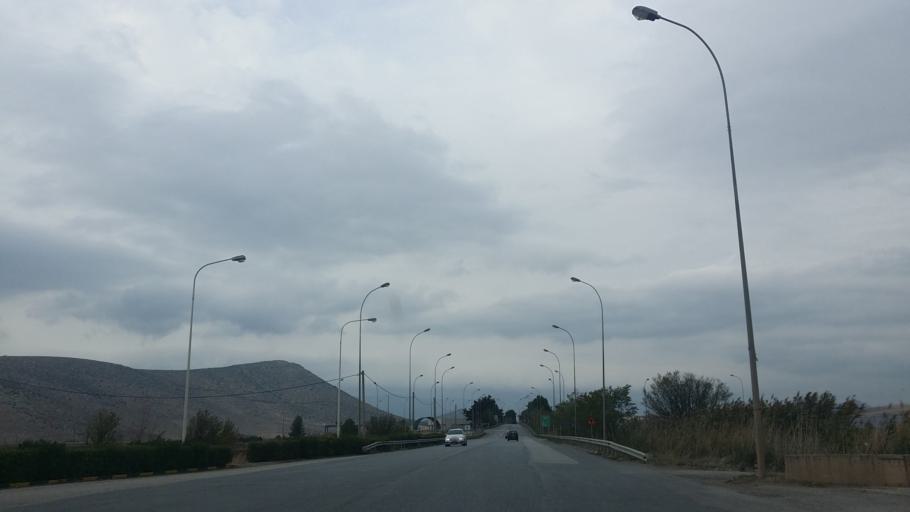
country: GR
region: Central Greece
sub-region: Nomos Voiotias
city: Thivai
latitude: 38.3602
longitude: 23.3224
